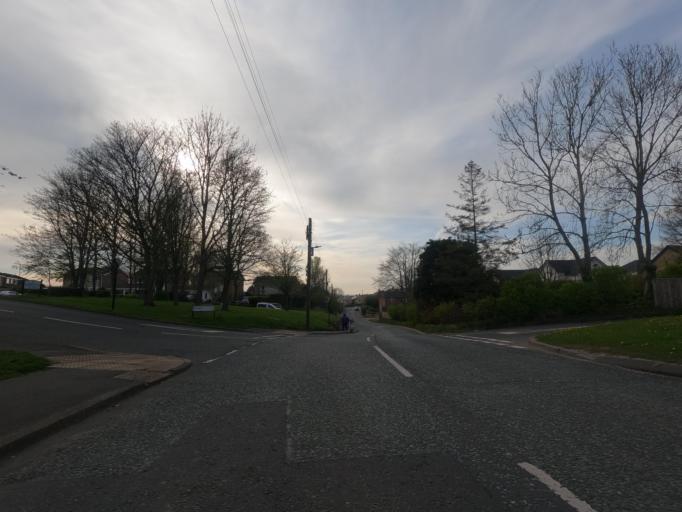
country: GB
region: England
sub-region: Newcastle upon Tyne
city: Dinnington
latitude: 55.0541
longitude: -1.6768
